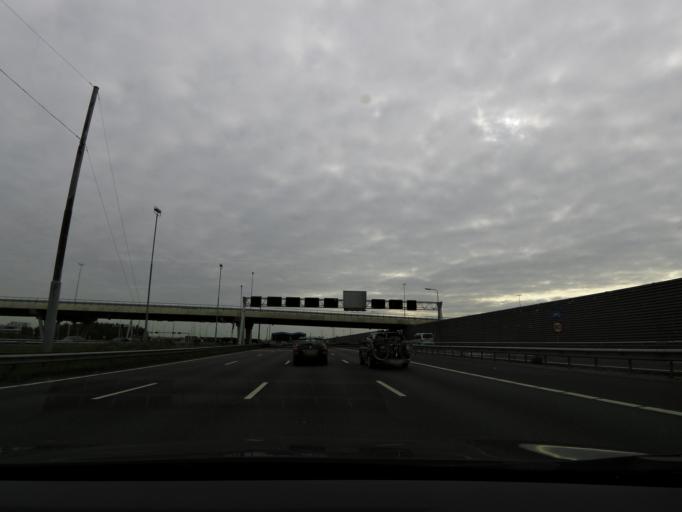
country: NL
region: North Holland
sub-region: Gemeente Aalsmeer
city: Aalsmeer
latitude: 52.3212
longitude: 4.7588
